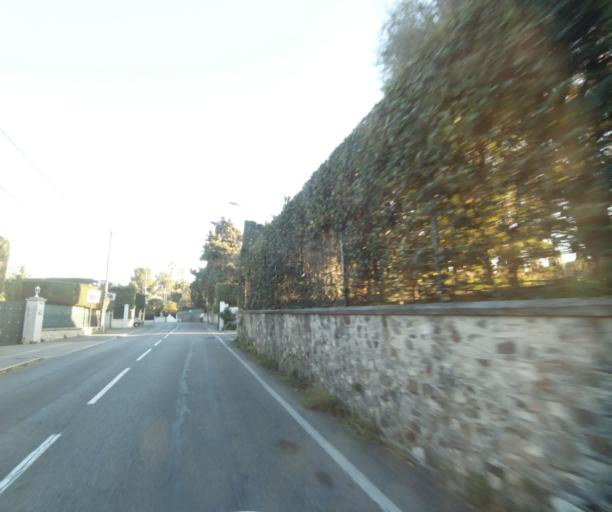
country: FR
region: Provence-Alpes-Cote d'Azur
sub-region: Departement des Alpes-Maritimes
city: Antibes
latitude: 43.5631
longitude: 7.1264
